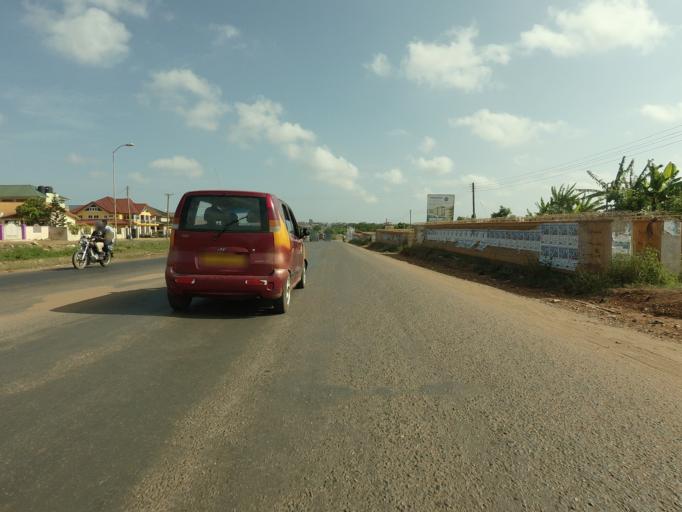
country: GH
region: Greater Accra
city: Tema
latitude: 5.6572
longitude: -0.0532
